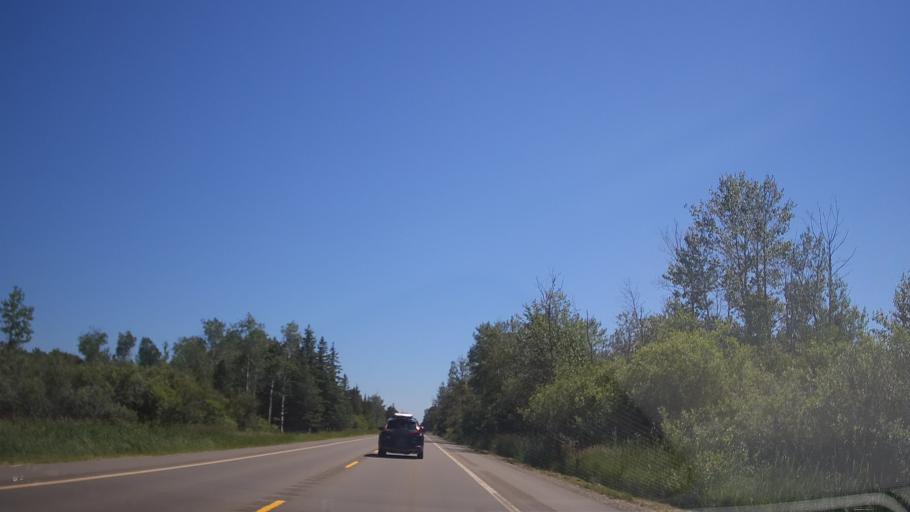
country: US
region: Michigan
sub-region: Cheboygan County
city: Indian River
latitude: 45.6076
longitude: -84.7822
